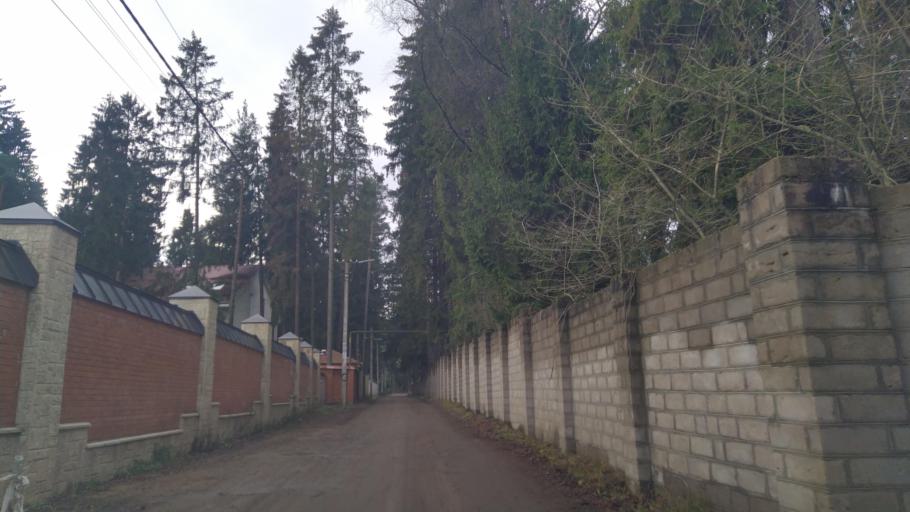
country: RU
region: Leningrad
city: Vsevolozhsk
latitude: 60.0228
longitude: 30.6733
